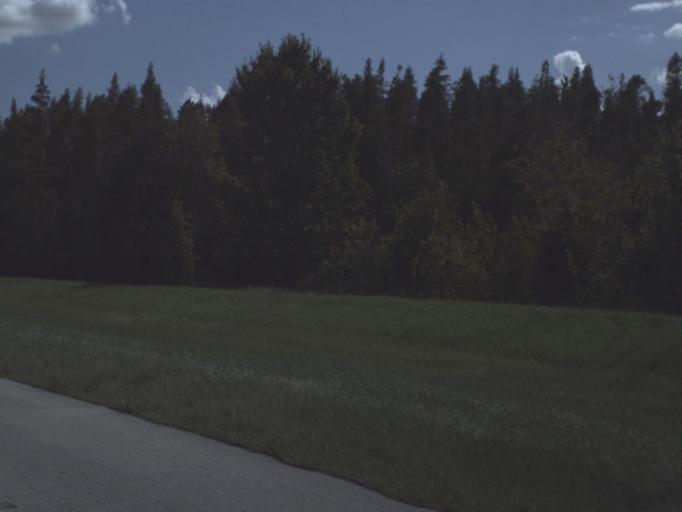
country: US
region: Florida
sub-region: Polk County
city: Winston
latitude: 28.0170
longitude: -82.0359
